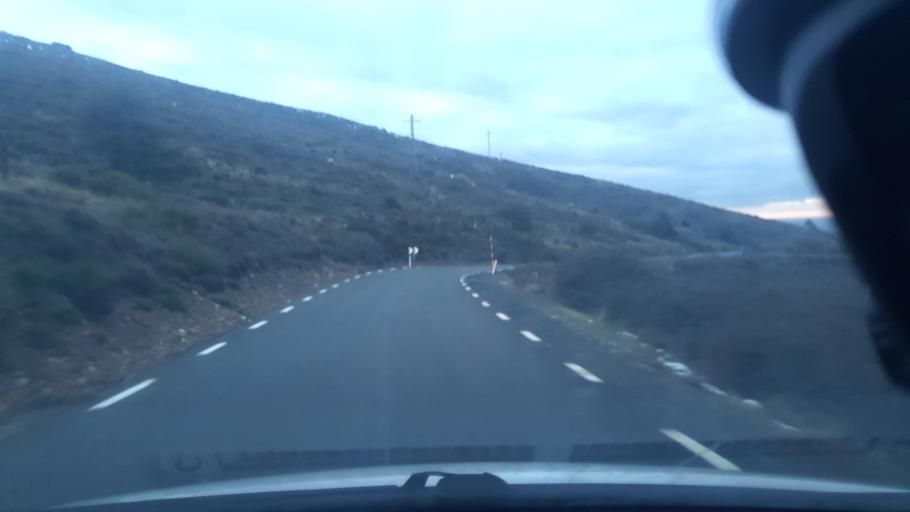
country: ES
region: Castille and Leon
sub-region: Provincia de Avila
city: Ojos-Albos
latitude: 40.7180
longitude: -4.4488
